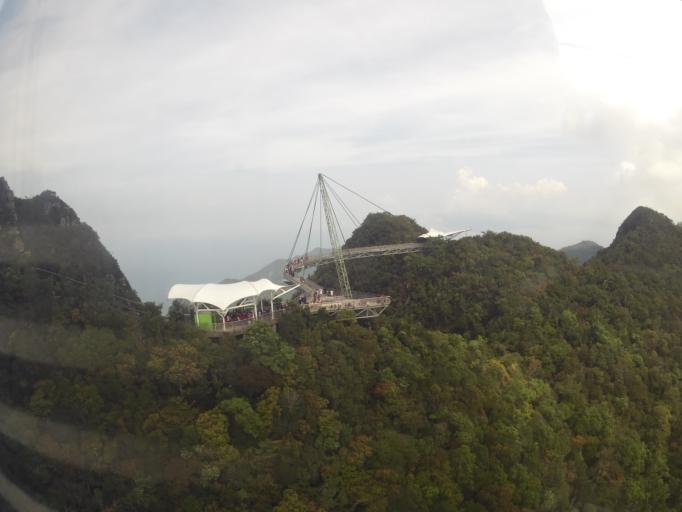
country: MY
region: Kedah
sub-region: Langkawi
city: Kuah
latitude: 6.3854
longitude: 99.6625
